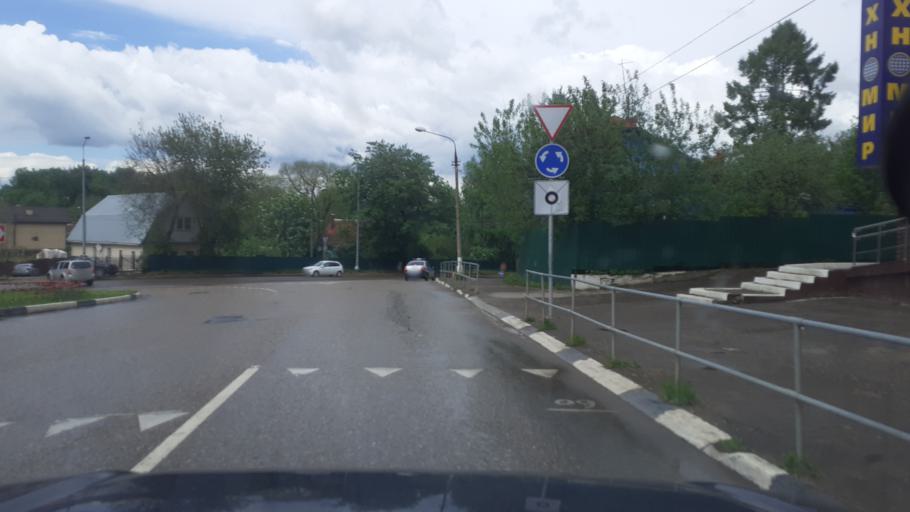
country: RU
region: Moskovskaya
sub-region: Volokolamskiy Rayon
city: Volokolamsk
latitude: 56.0318
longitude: 35.9589
